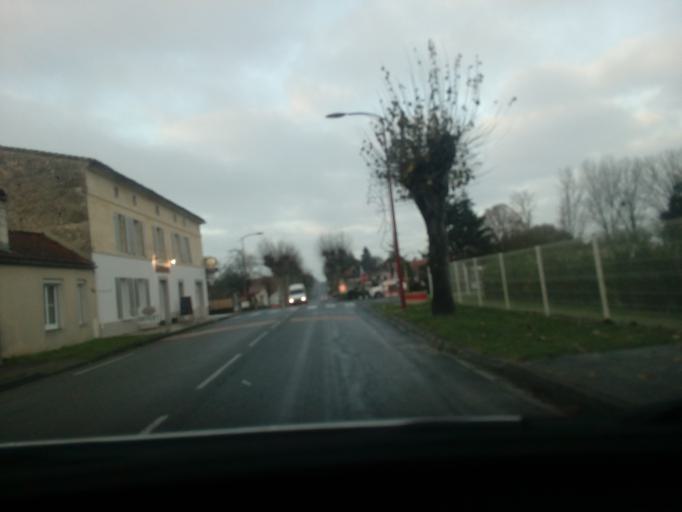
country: FR
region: Poitou-Charentes
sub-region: Departement de la Charente
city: Baignes-Sainte-Radegonde
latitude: 45.4435
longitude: -0.2987
